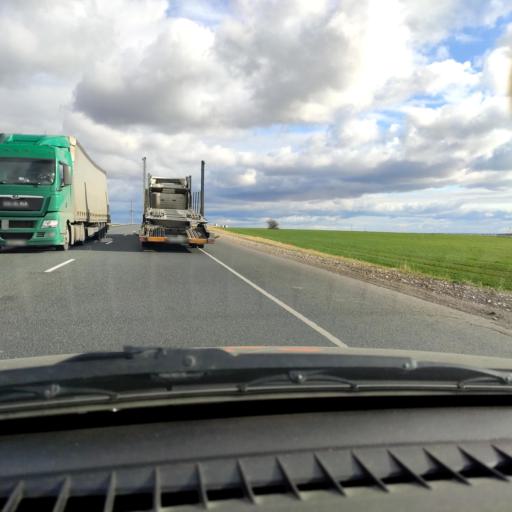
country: RU
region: Samara
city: Varlamovo
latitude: 53.2094
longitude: 48.3923
